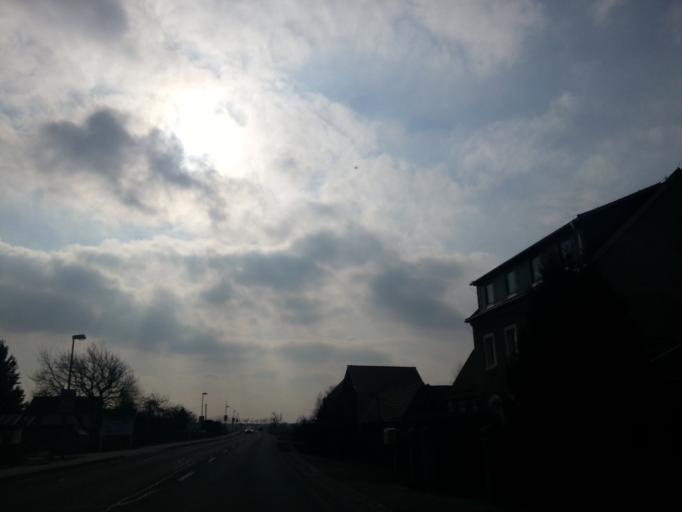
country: DE
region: Saxony
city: Niederschona
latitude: 50.9789
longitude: 13.4443
